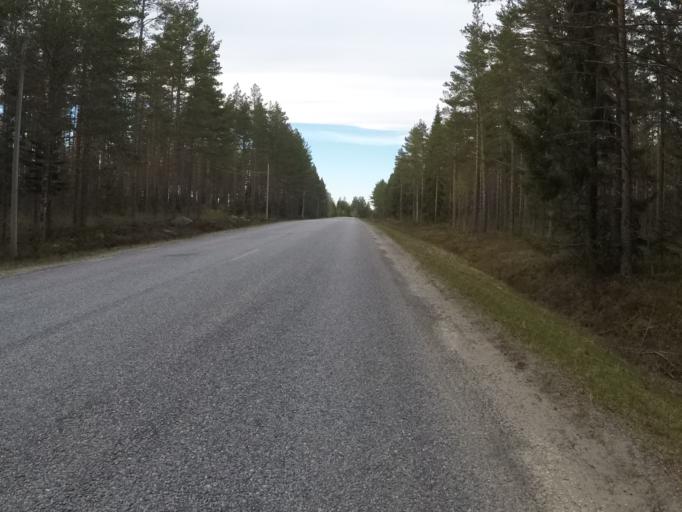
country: SE
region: Vaesterbotten
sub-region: Umea Kommun
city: Saevar
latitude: 63.9346
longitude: 20.7824
